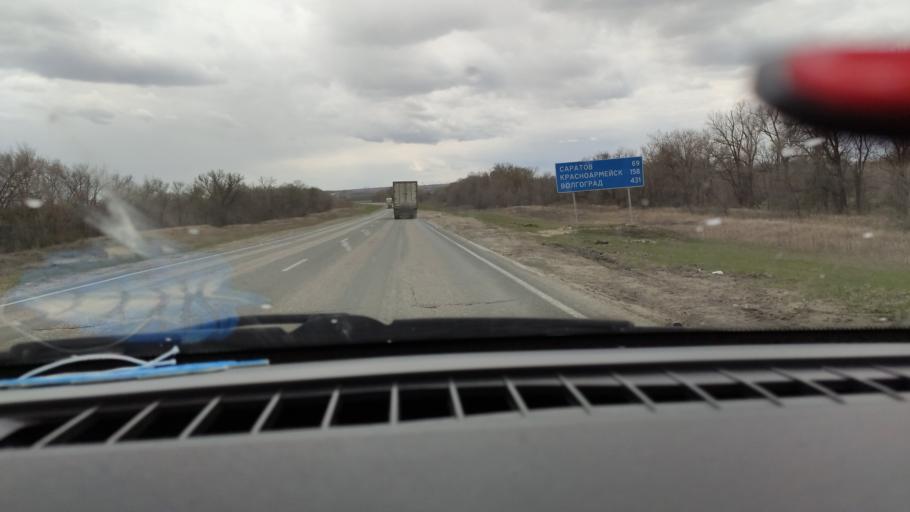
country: RU
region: Saratov
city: Sinodskoye
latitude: 51.9771
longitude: 46.6493
